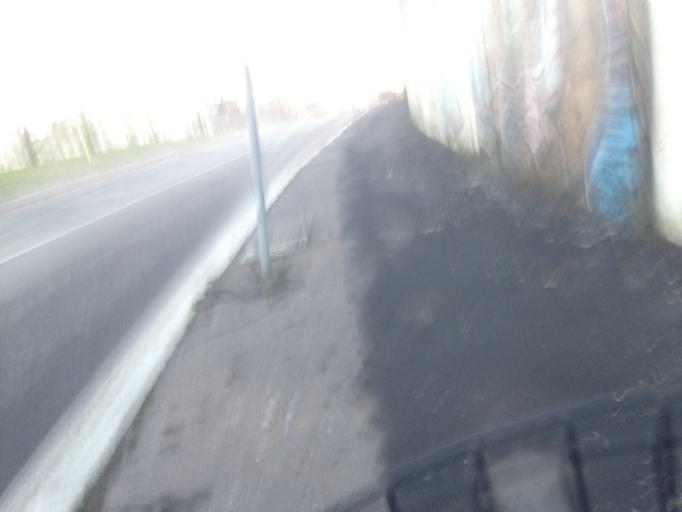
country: IT
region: Lombardy
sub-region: Citta metropolitana di Milano
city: Milano
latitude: 45.4303
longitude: 9.1666
